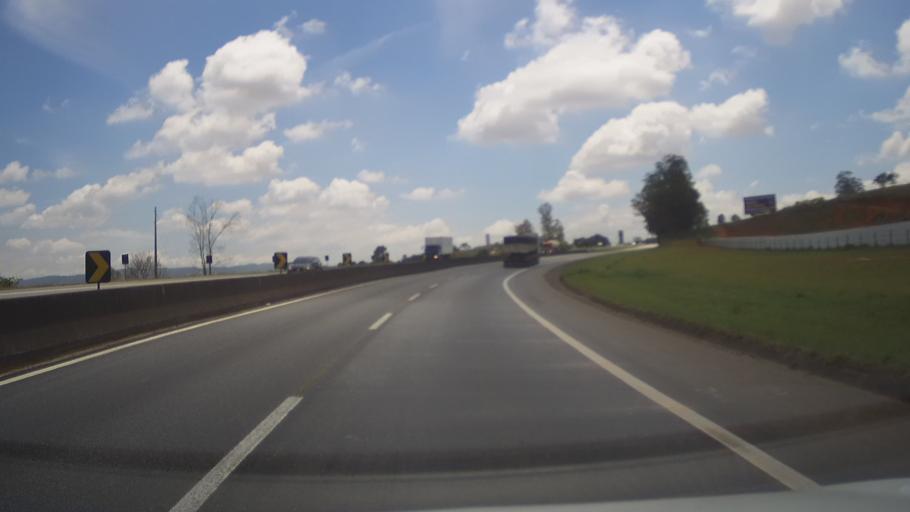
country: BR
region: Minas Gerais
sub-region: Sao Goncalo Do Sapucai
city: Sao Goncalo do Sapucai
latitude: -21.9503
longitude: -45.6241
